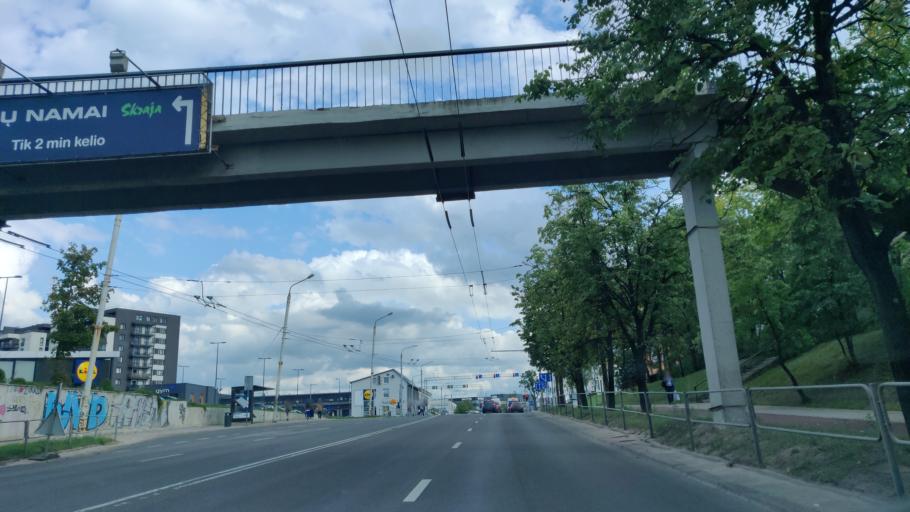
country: LT
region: Vilnius County
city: Vilkpede
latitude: 54.6730
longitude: 25.2549
